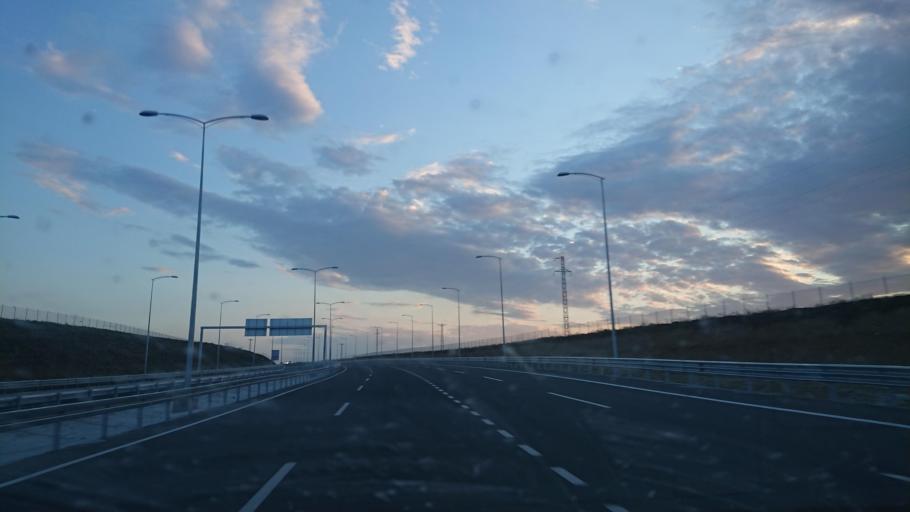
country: TR
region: Aksaray
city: Balci
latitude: 38.7702
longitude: 34.1009
